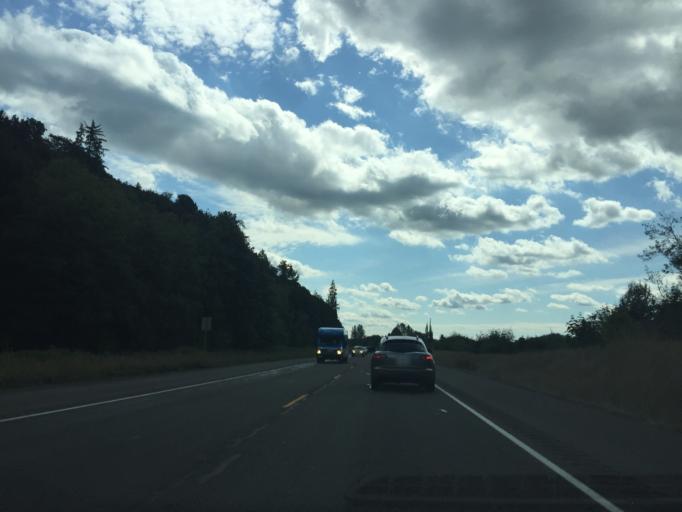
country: US
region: Washington
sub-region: Snohomish County
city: Snohomish
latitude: 47.9258
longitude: -122.0736
